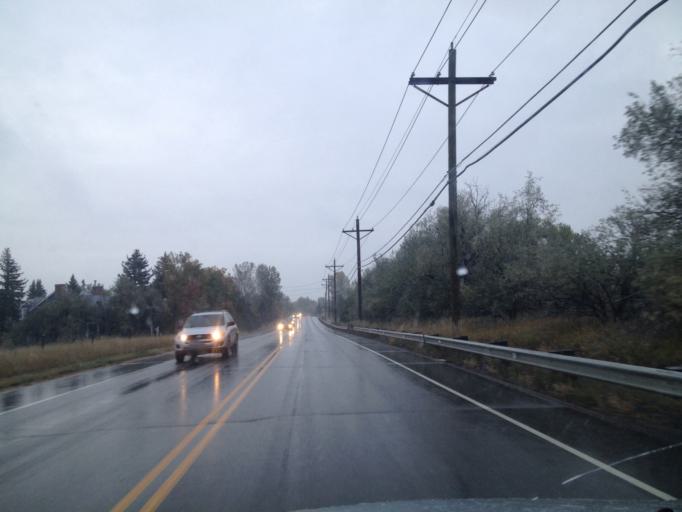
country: US
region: Colorado
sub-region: Boulder County
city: Superior
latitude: 39.9958
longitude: -105.1751
